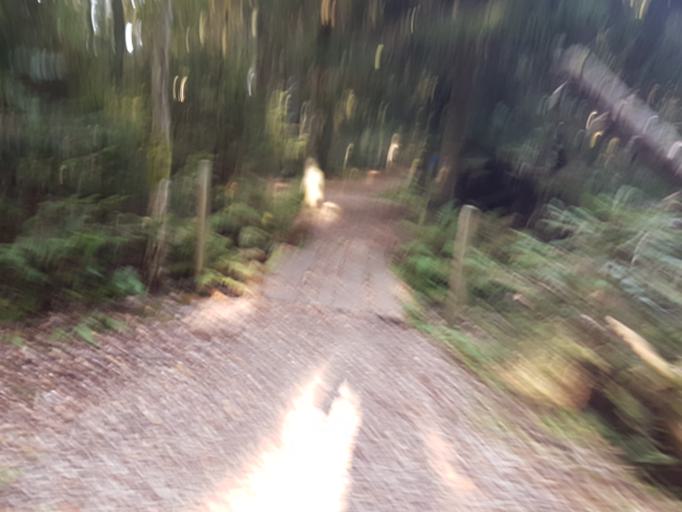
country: SE
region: Kronoberg
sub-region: Vaxjo Kommun
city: Vaexjoe
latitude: 56.8514
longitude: 14.8387
